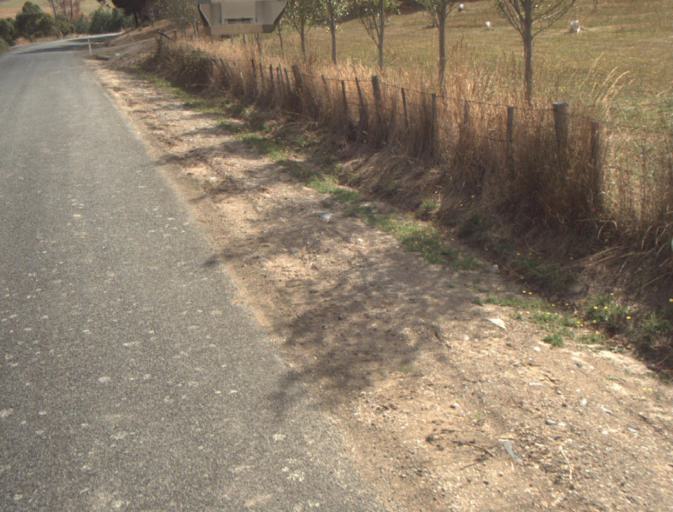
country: AU
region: Tasmania
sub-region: Launceston
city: Mayfield
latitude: -41.2584
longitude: 147.2080
